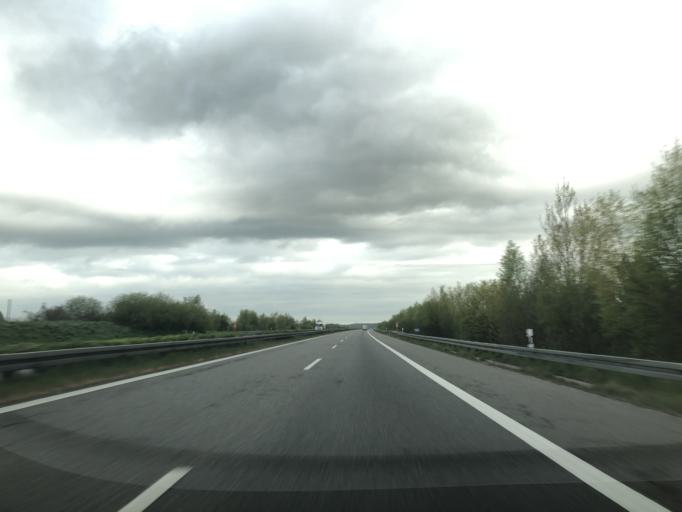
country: DE
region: Mecklenburg-Vorpommern
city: Tessin
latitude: 54.0194
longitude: 12.4328
